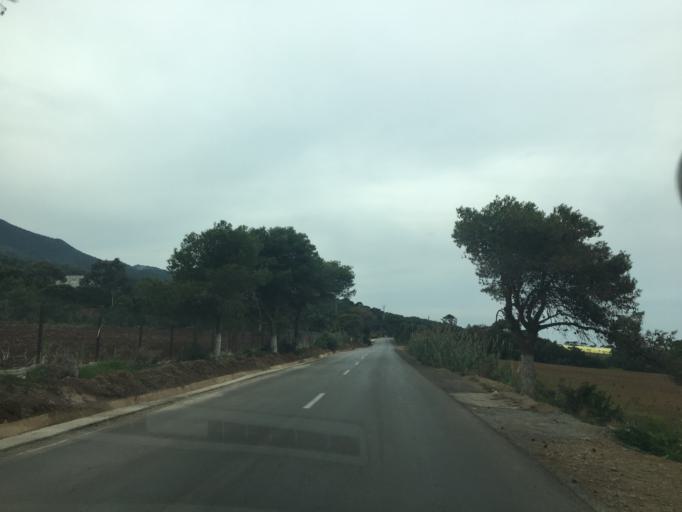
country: DZ
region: Tipaza
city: Tipasa
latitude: 36.6334
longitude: 2.3953
